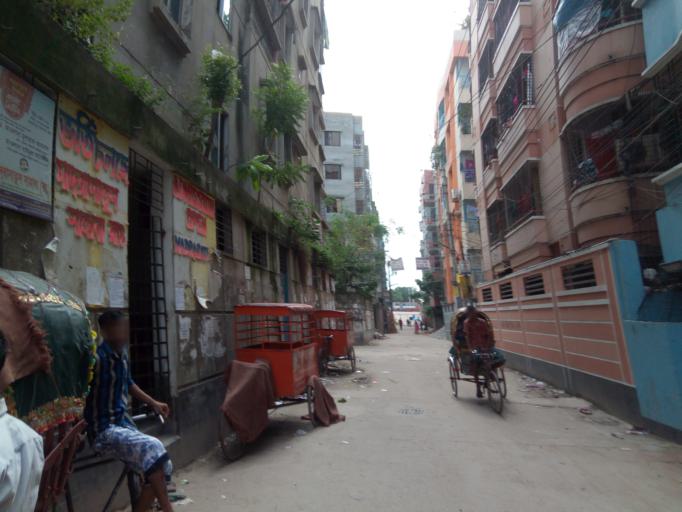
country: BD
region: Dhaka
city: Azimpur
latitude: 23.7409
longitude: 90.3620
